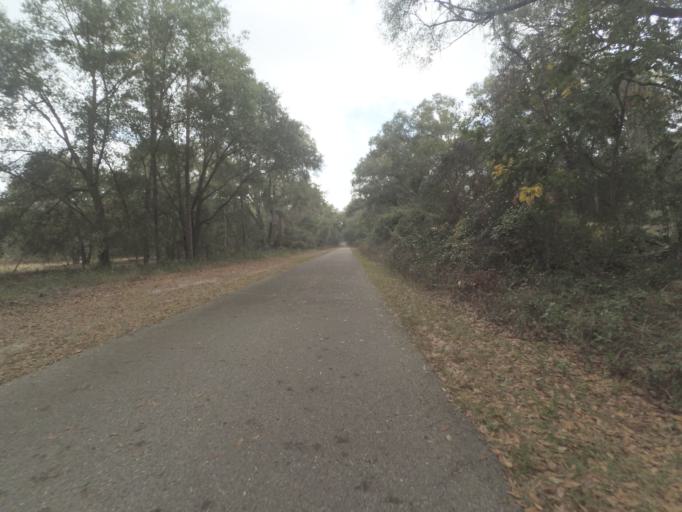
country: US
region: Florida
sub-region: Alachua County
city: Gainesville
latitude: 29.6178
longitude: -82.3086
